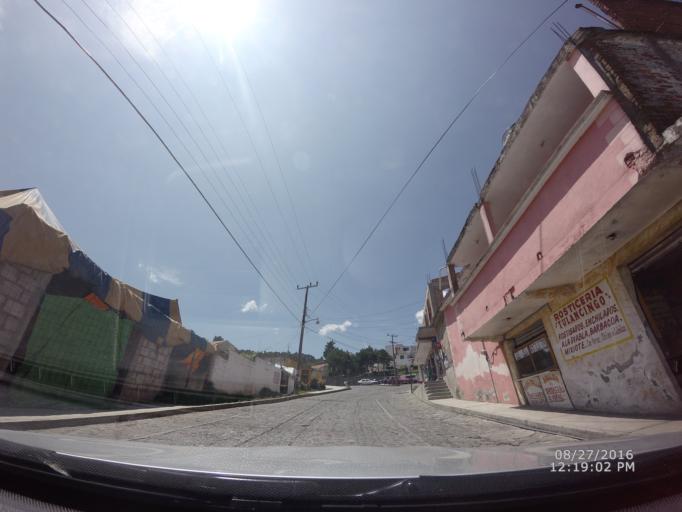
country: MX
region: Hidalgo
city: Mineral del Monte
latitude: 20.1367
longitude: -98.6706
